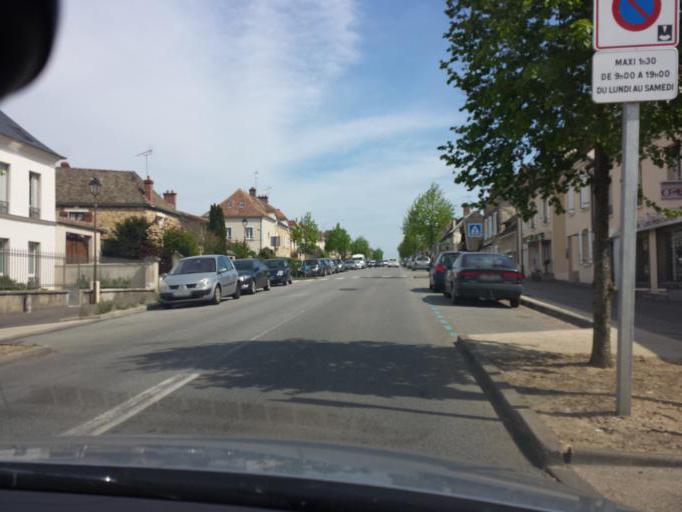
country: FR
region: Ile-de-France
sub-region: Departement des Yvelines
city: Neauphle-le-Chateau
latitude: 48.8037
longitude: 1.8973
